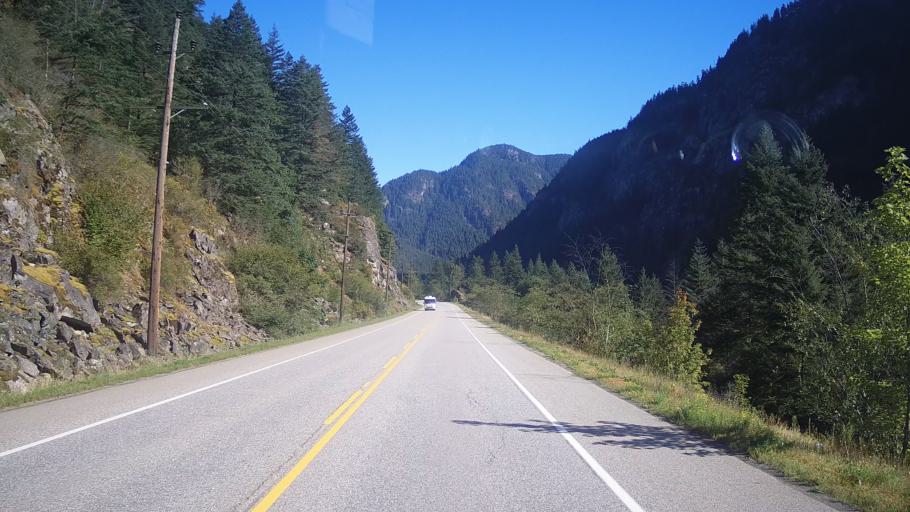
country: CA
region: British Columbia
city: Hope
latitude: 49.5844
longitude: -121.4041
